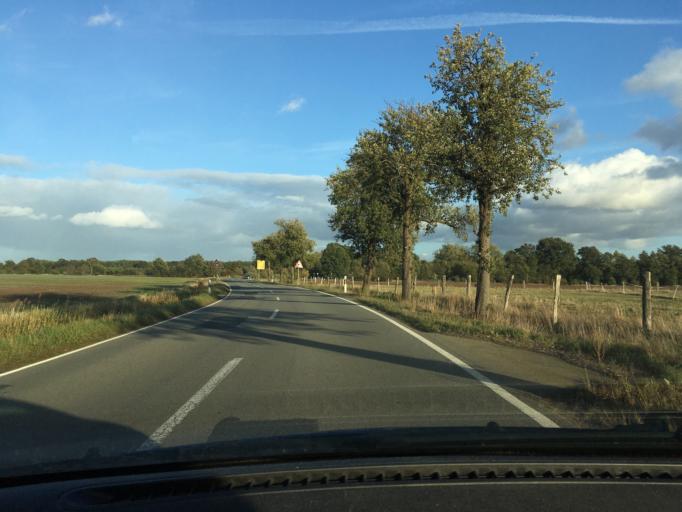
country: DE
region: Lower Saxony
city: Hittbergen
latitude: 53.3423
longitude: 10.6030
